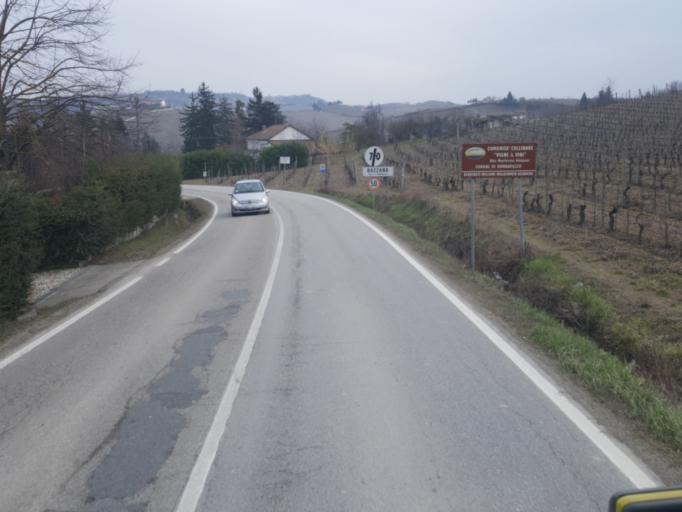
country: IT
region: Piedmont
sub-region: Provincia di Asti
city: Castelnuovo Belbo
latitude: 44.7764
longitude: 8.3959
